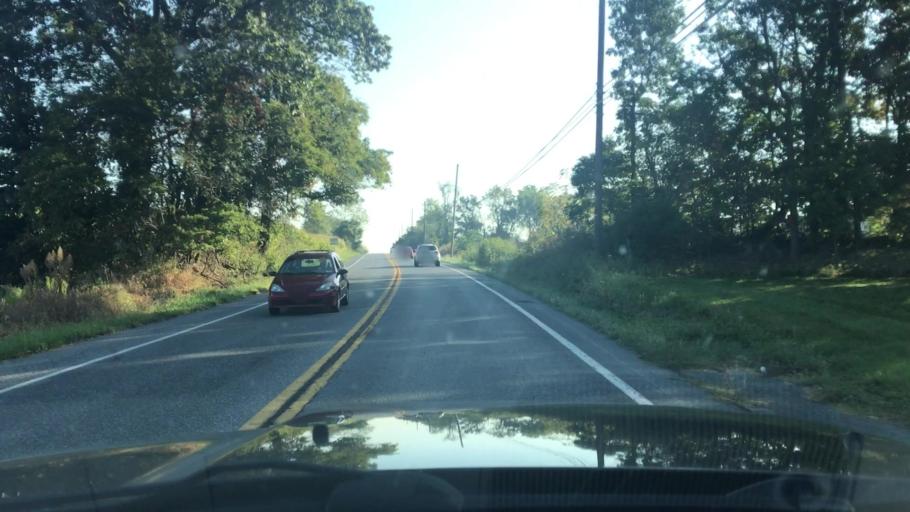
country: US
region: Pennsylvania
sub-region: Berks County
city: Topton
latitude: 40.4848
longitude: -75.7334
